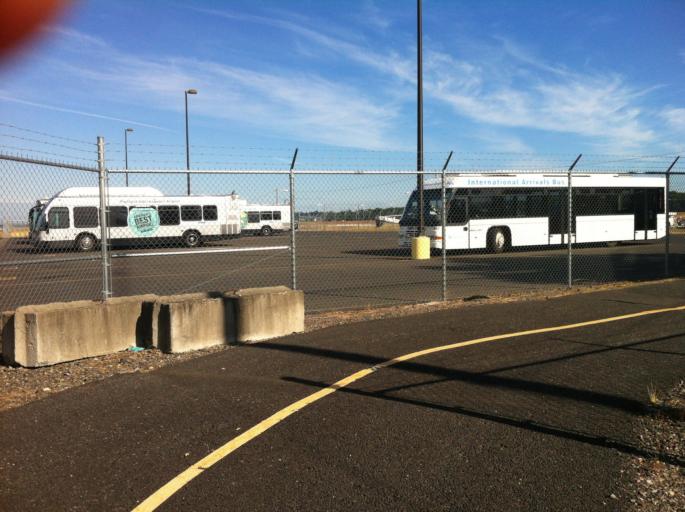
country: US
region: Washington
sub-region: Clark County
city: Orchards
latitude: 45.5785
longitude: -122.5607
